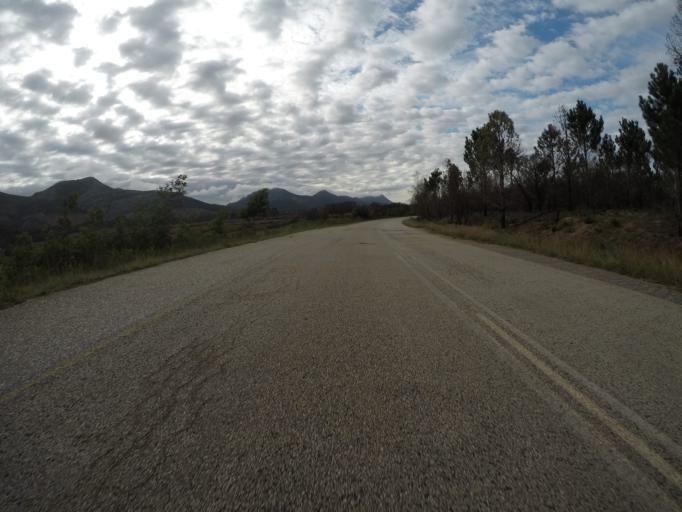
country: ZA
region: Eastern Cape
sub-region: Cacadu District Municipality
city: Kareedouw
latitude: -34.0116
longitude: 24.3113
